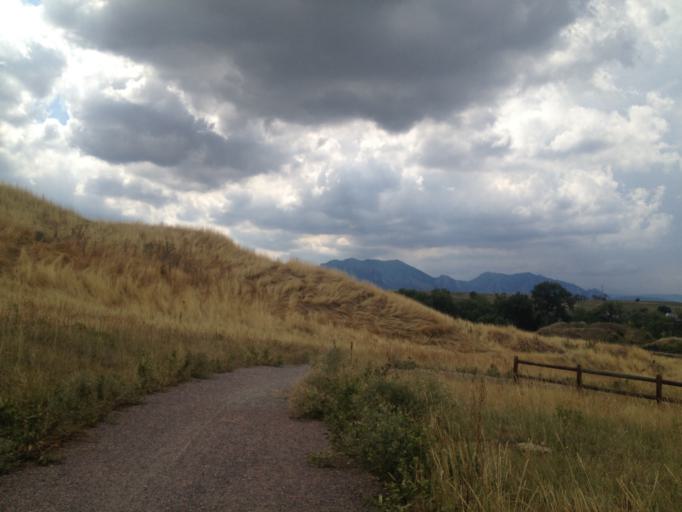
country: US
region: Colorado
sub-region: Boulder County
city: Superior
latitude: 39.9480
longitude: -105.1695
